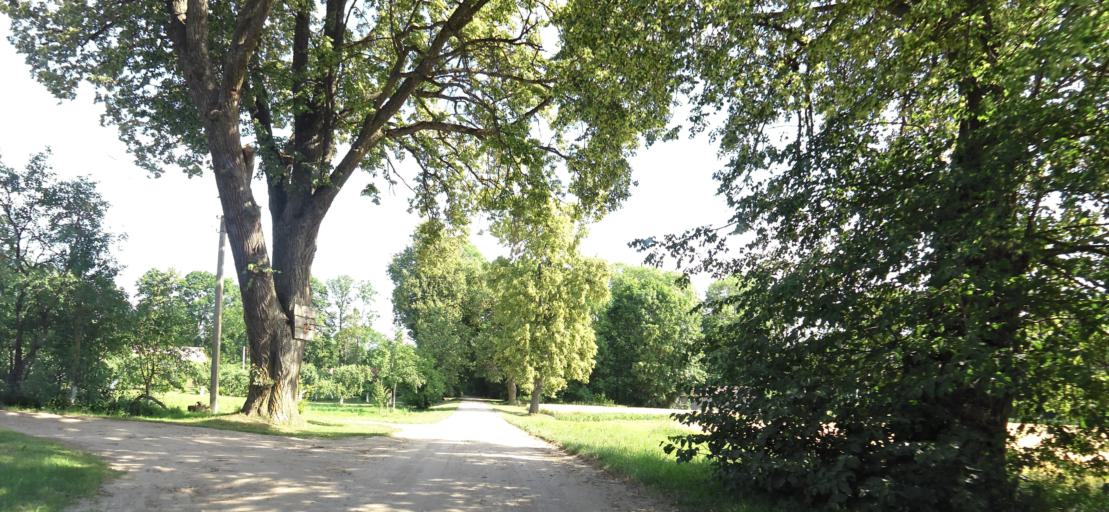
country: LT
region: Panevezys
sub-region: Birzai
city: Birzai
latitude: 56.2133
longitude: 24.6811
